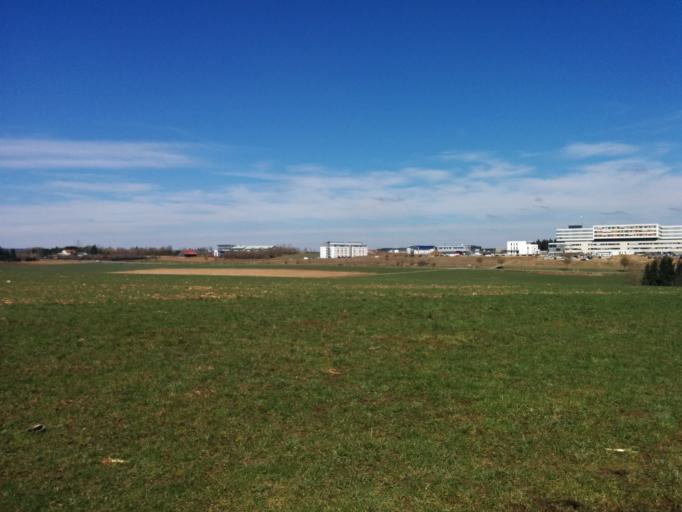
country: DE
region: Baden-Wuerttemberg
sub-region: Freiburg Region
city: Villingen-Schwenningen
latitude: 48.0590
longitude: 8.4997
